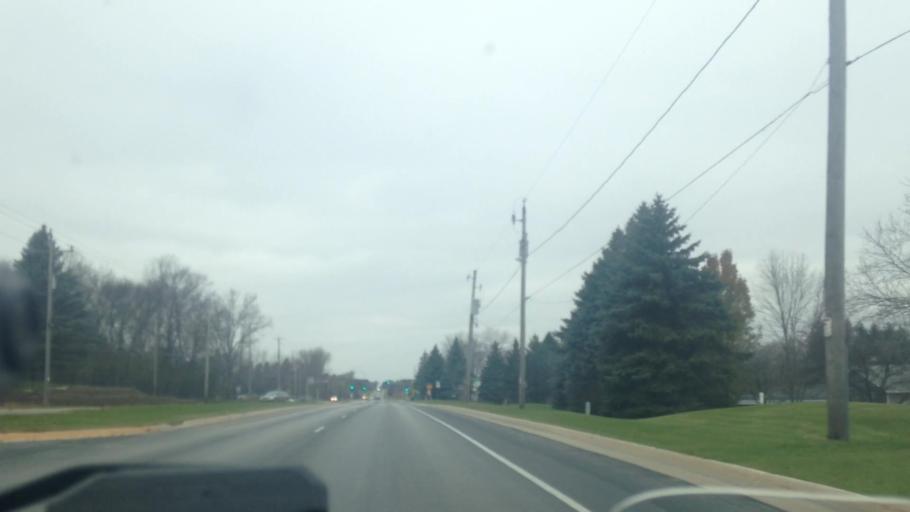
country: US
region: Wisconsin
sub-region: Waukesha County
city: Lannon
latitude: 43.1929
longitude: -88.1785
